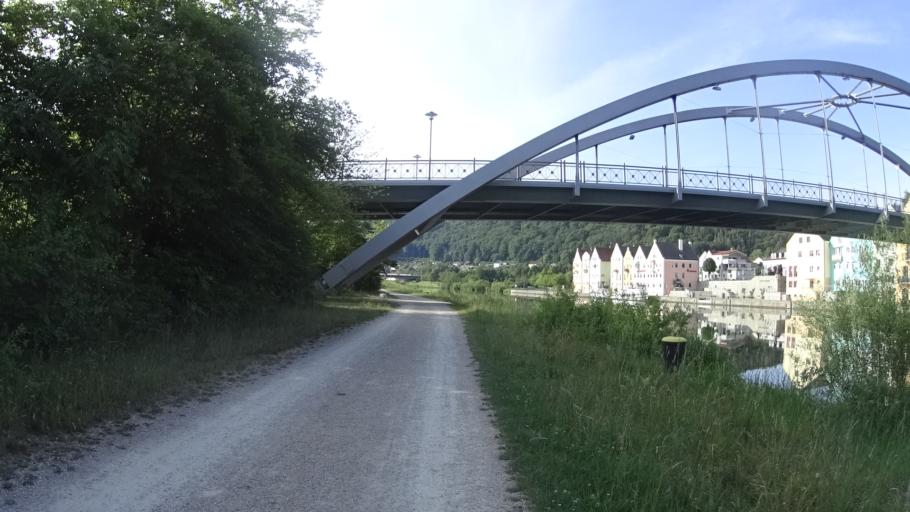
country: DE
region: Bavaria
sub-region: Lower Bavaria
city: Riedenburg
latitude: 48.9639
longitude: 11.6848
